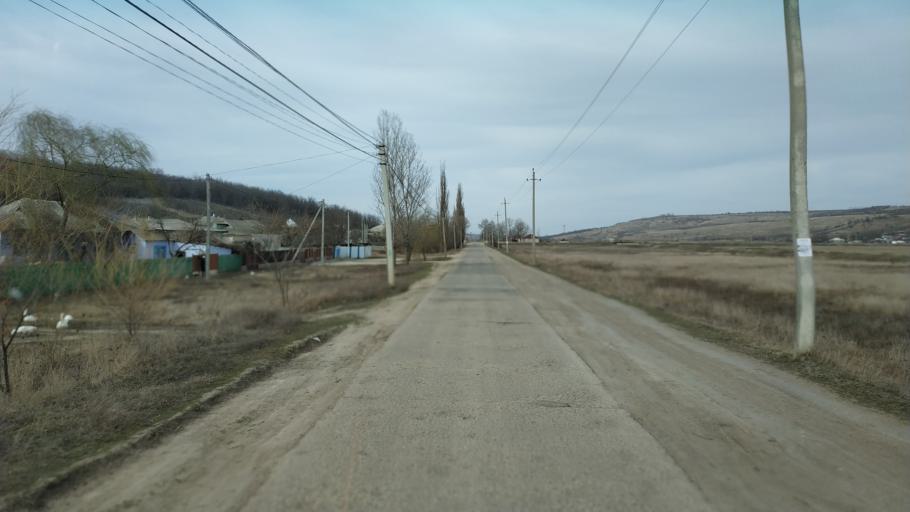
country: RO
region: Vaslui
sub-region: Comuna Dranceni
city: Dranceni
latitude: 46.8685
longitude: 28.1994
